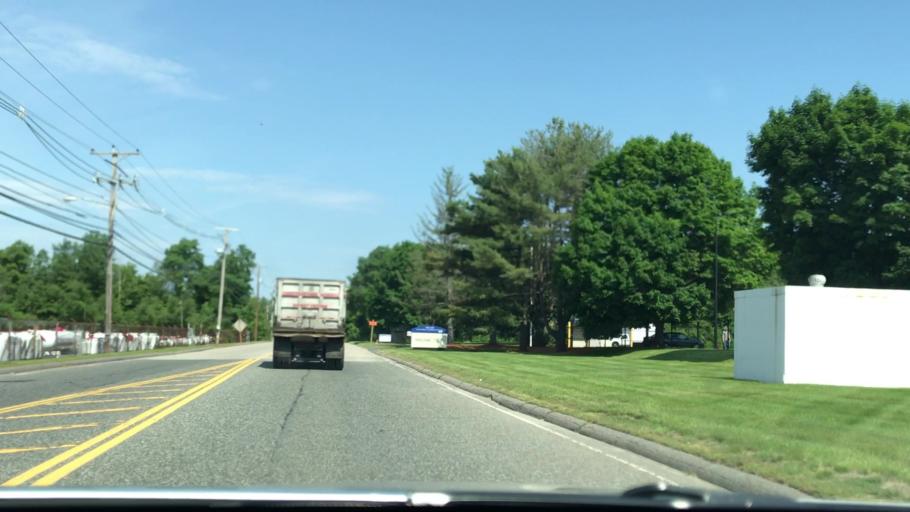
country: US
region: Massachusetts
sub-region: Middlesex County
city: Marlborough
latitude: 42.3175
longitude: -71.5817
